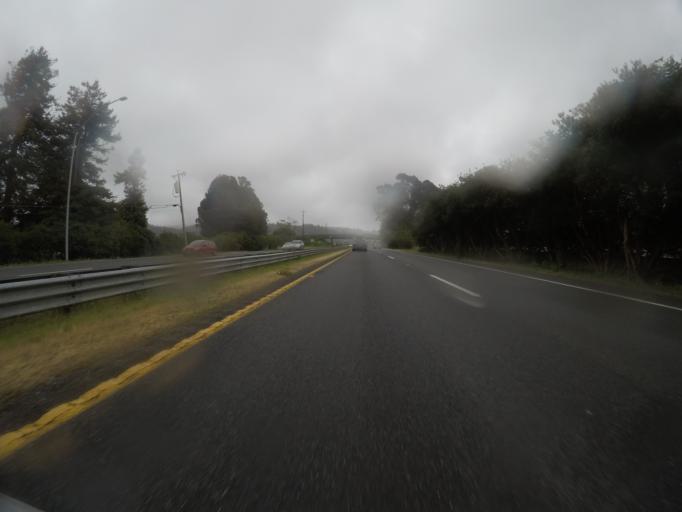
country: US
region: California
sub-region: Humboldt County
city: Arcata
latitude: 40.8988
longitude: -124.0841
